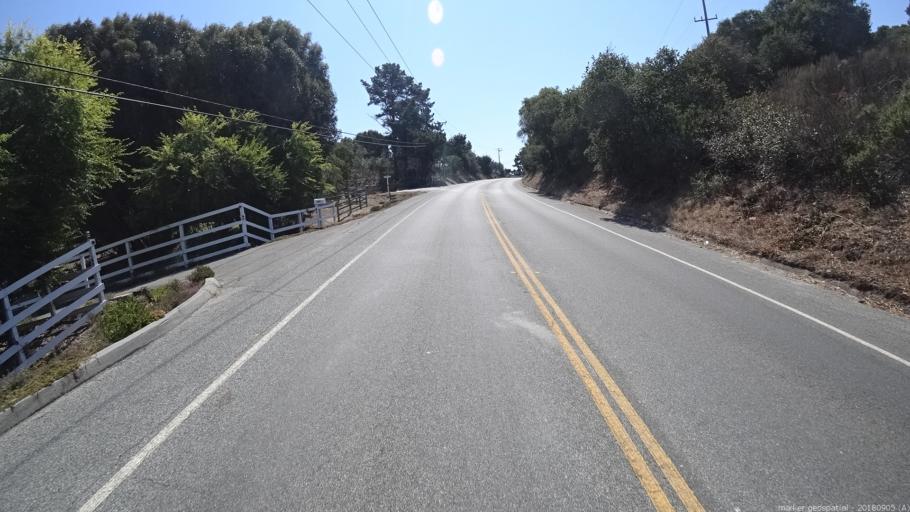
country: US
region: California
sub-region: Monterey County
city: Carmel Valley Village
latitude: 36.5490
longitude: -121.7529
